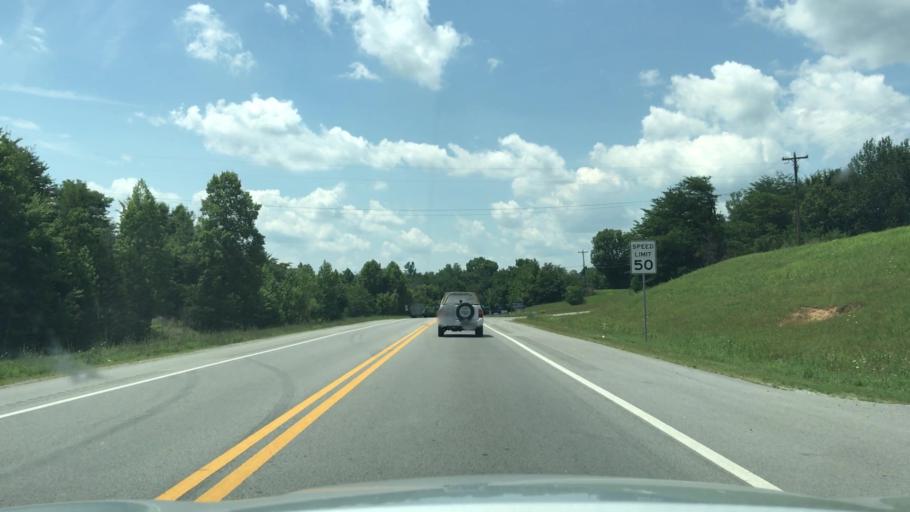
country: US
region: Tennessee
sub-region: Pickett County
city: Byrdstown
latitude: 36.5881
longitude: -85.1259
